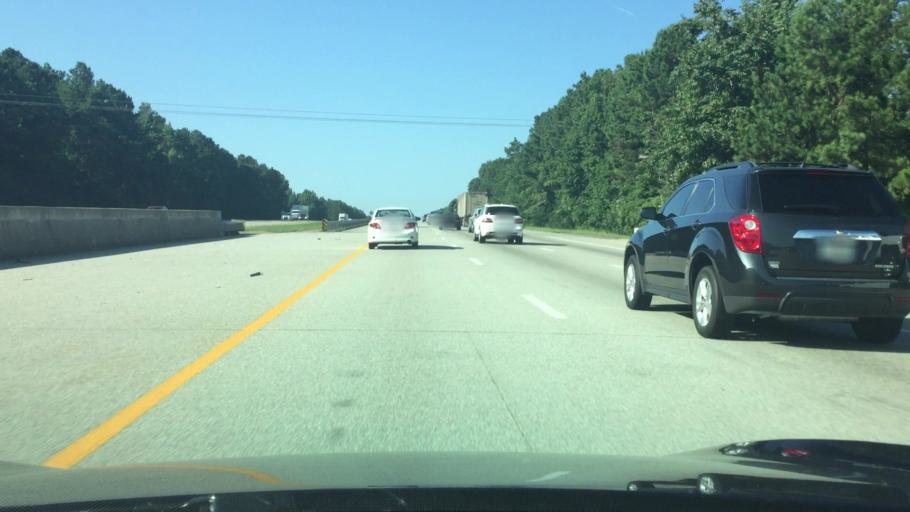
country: US
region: Georgia
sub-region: Coweta County
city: Grantville
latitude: 33.2830
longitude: -84.7990
